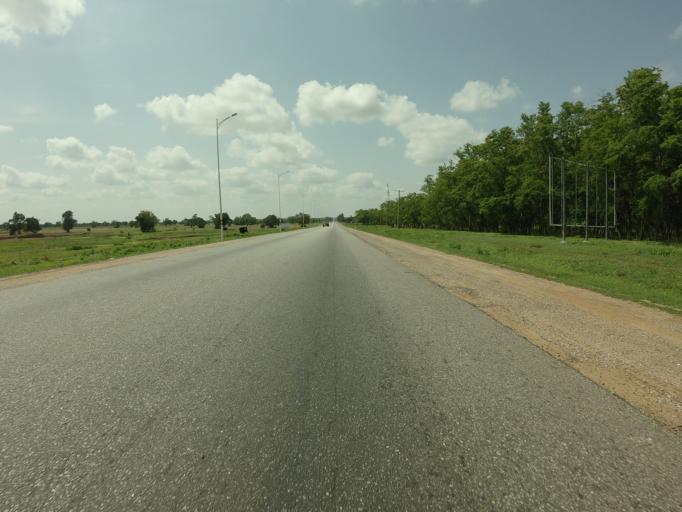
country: GH
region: Northern
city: Savelugu
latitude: 9.5412
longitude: -0.8390
